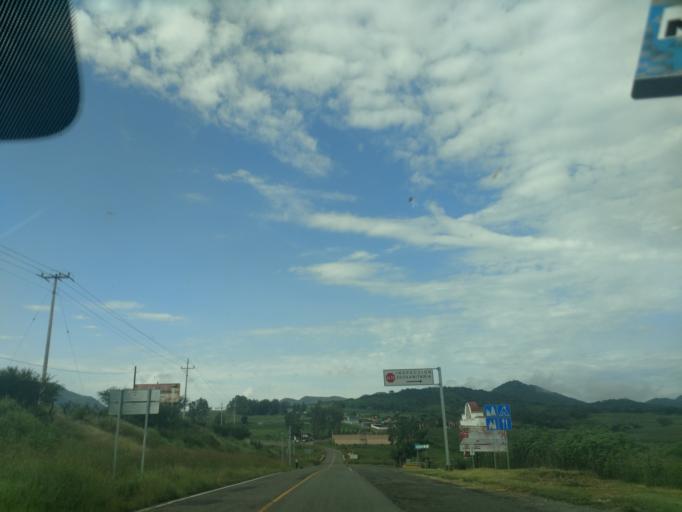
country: MX
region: Jalisco
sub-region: Atengo
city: Soyatlan del Oro
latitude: 20.5264
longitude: -104.3356
